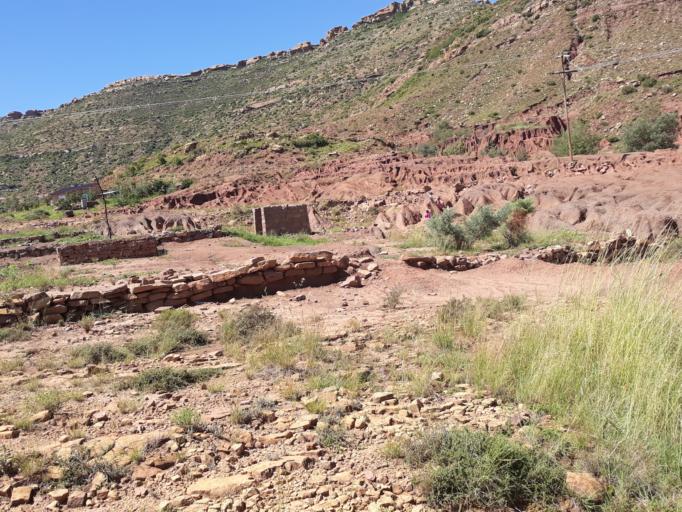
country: LS
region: Quthing
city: Quthing
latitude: -30.3341
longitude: 27.5357
